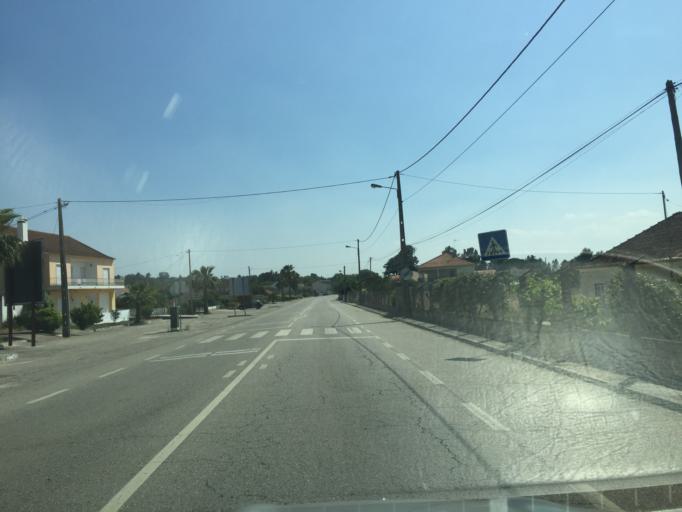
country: PT
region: Santarem
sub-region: Chamusca
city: Vila Nova da Barquinha
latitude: 39.4153
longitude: -8.4211
